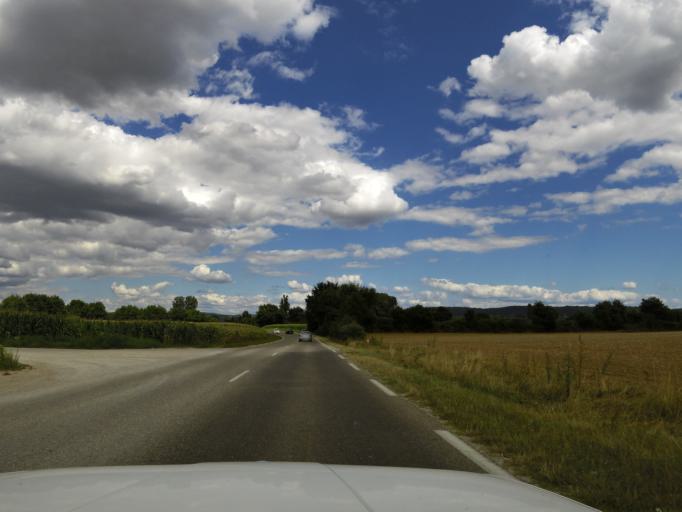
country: FR
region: Rhone-Alpes
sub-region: Departement de l'Isere
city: Saint-Romain-de-Jalionas
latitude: 45.7532
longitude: 5.2028
